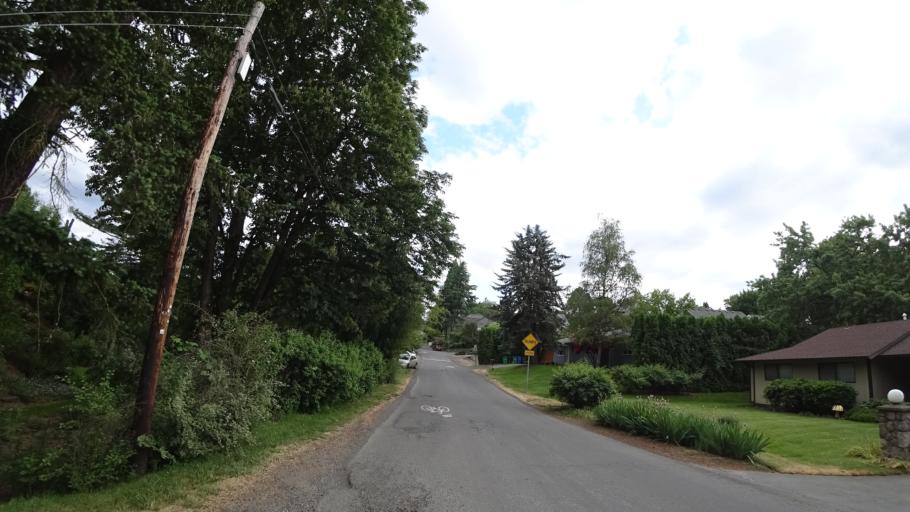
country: US
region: Oregon
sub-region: Washington County
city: Garden Home-Whitford
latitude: 45.4762
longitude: -122.7306
